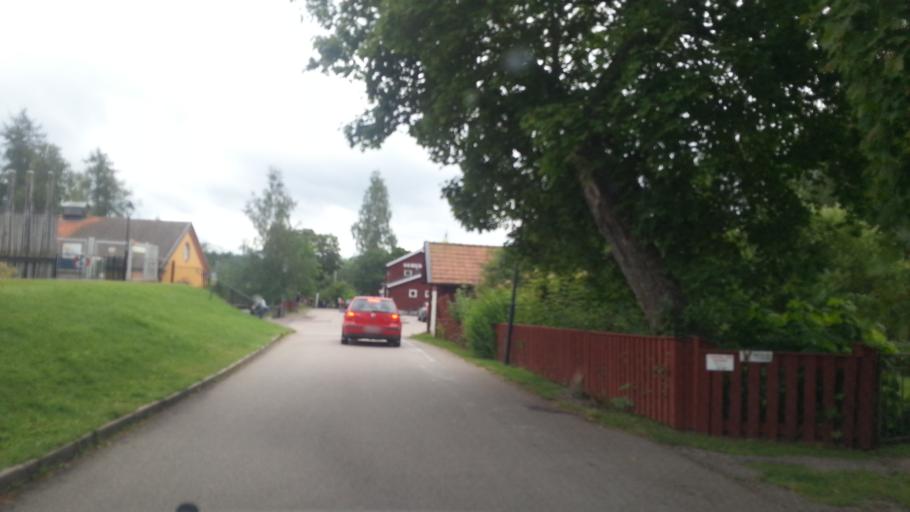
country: SE
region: Dalarna
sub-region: Faluns Kommun
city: Falun
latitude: 60.6517
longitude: 15.7761
